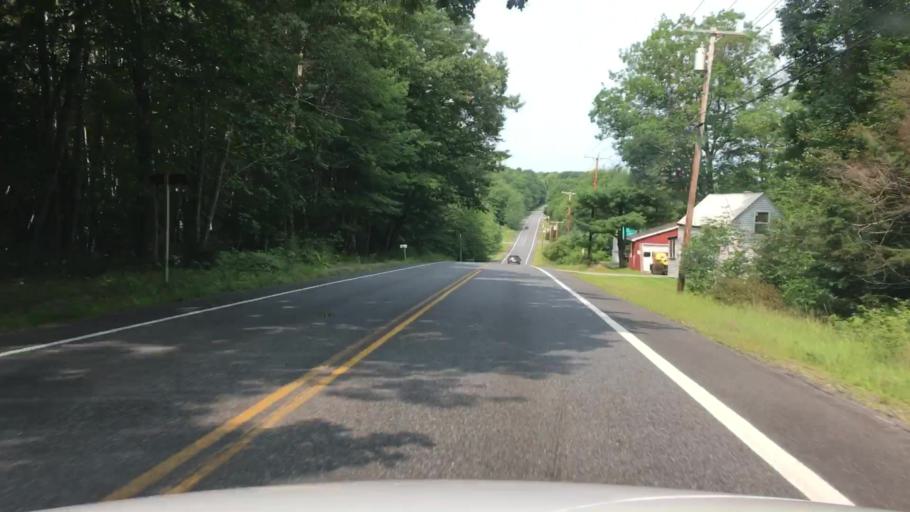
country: US
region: Maine
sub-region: Kennebec County
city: Winthrop
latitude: 44.3232
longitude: -69.9837
